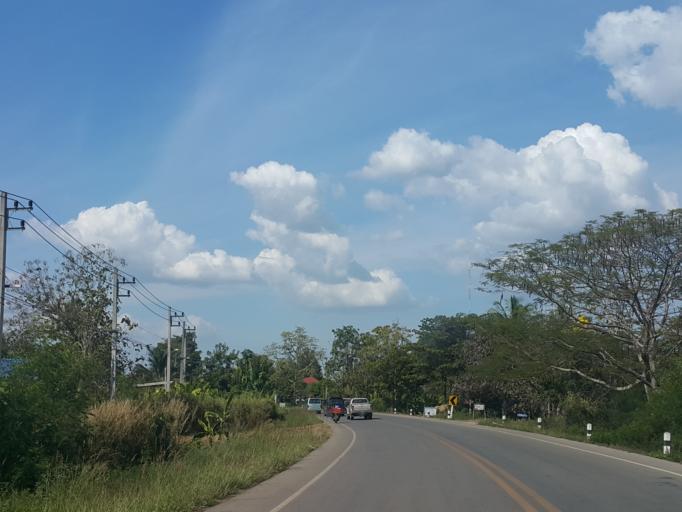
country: TH
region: Sukhothai
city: Sawankhalok
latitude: 17.2860
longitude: 99.8346
